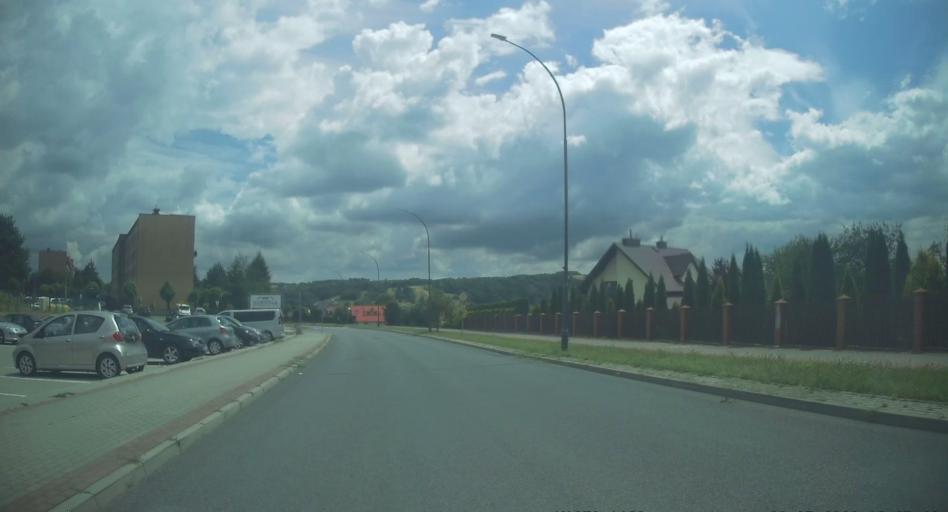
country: PL
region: Subcarpathian Voivodeship
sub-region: Powiat ropczycko-sedziszowski
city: Ropczyce
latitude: 50.0569
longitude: 21.6003
